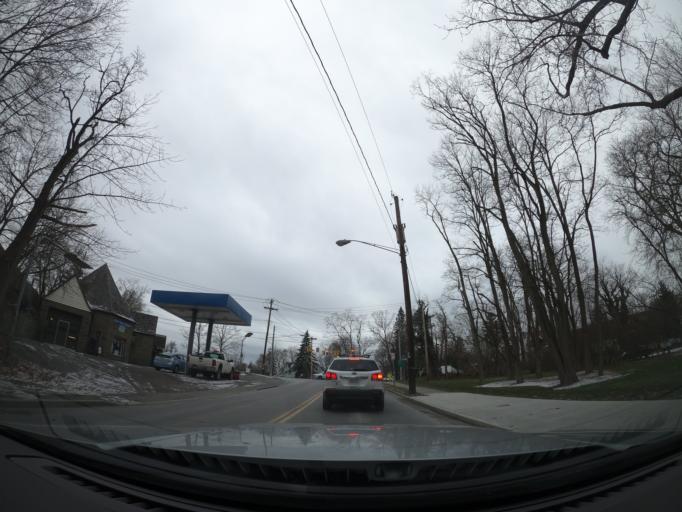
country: US
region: New York
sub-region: Tompkins County
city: East Ithaca
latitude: 42.4416
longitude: -76.4774
